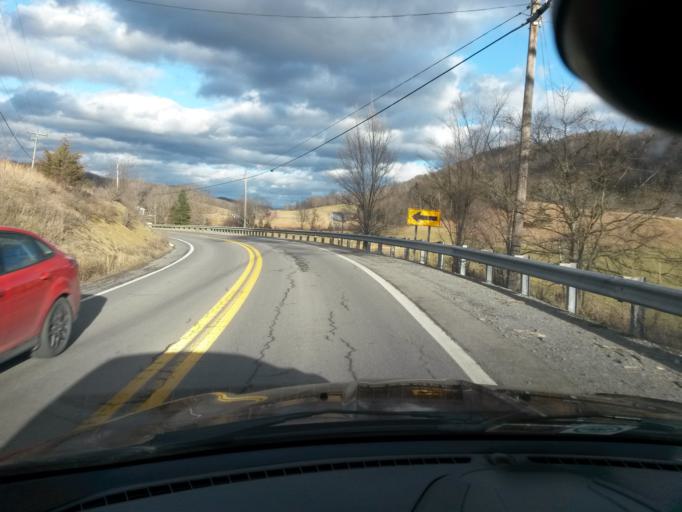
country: US
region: Virginia
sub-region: Giles County
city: Pembroke
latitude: 37.4580
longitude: -80.6632
